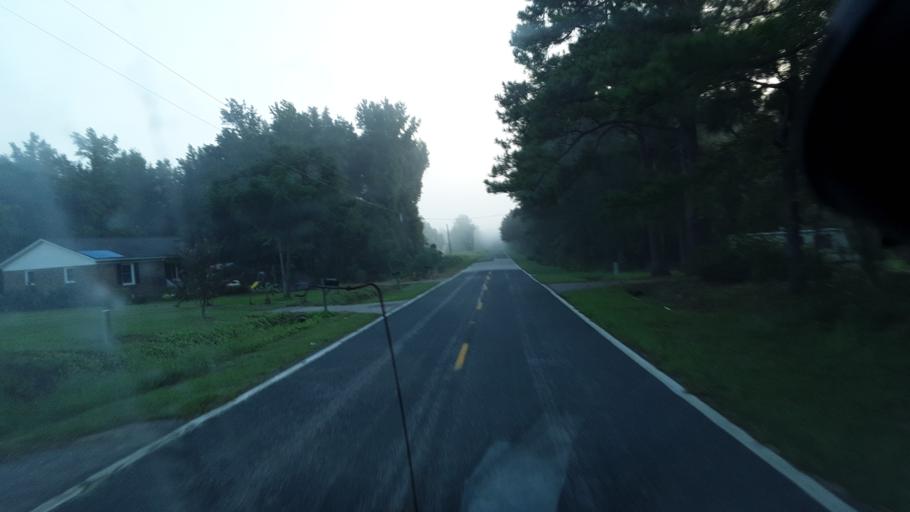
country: US
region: South Carolina
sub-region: Clarendon County
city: Manning
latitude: 33.7402
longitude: -80.0809
